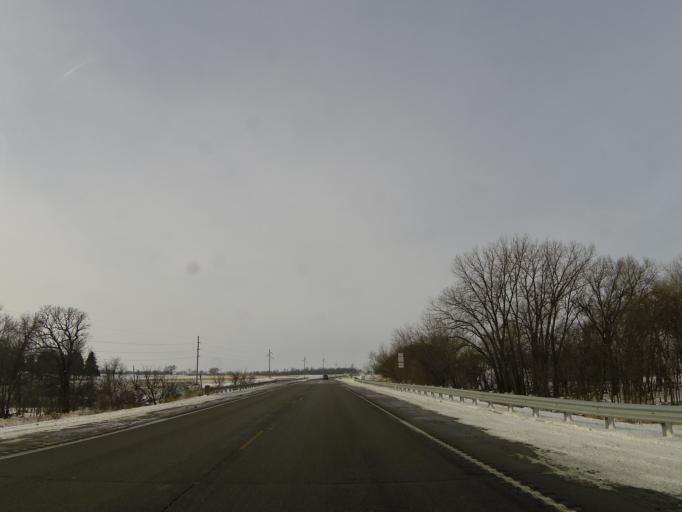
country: US
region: Minnesota
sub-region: Carver County
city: Mayer
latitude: 44.9056
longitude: -93.8838
